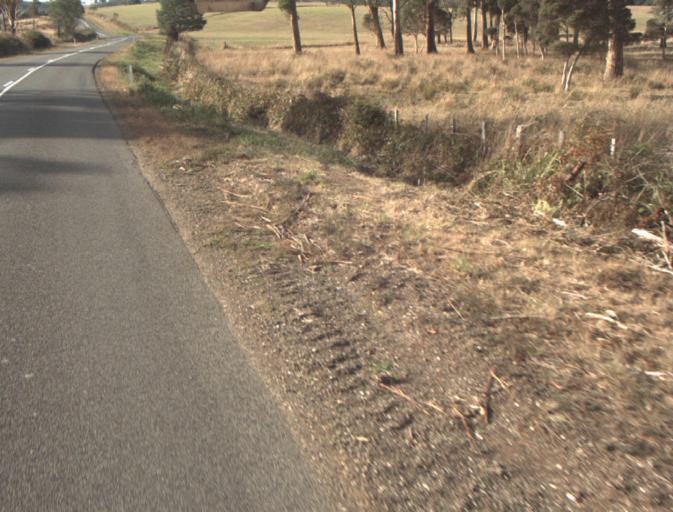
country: AU
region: Tasmania
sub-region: Launceston
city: Mayfield
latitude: -41.2201
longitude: 147.1215
